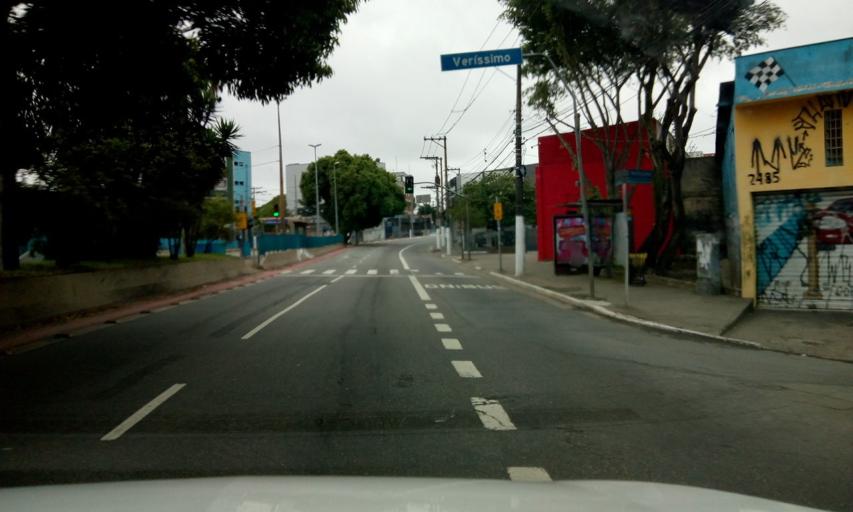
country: BR
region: Sao Paulo
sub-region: Diadema
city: Diadema
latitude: -23.6499
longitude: -46.6404
